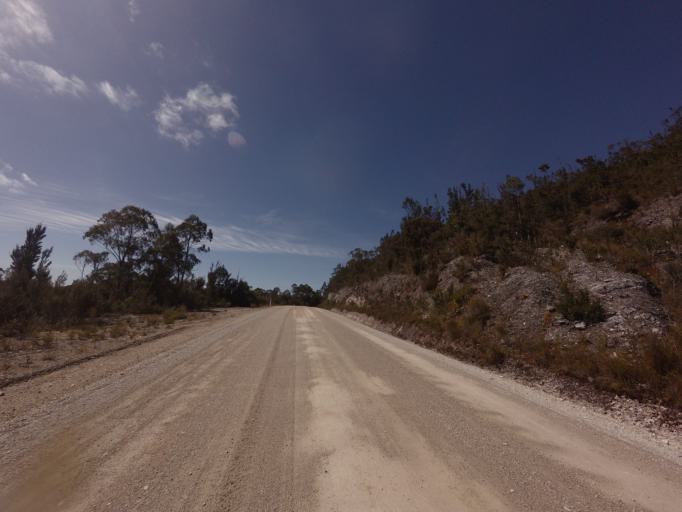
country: AU
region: Tasmania
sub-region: Huon Valley
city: Geeveston
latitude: -42.8198
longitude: 146.3885
